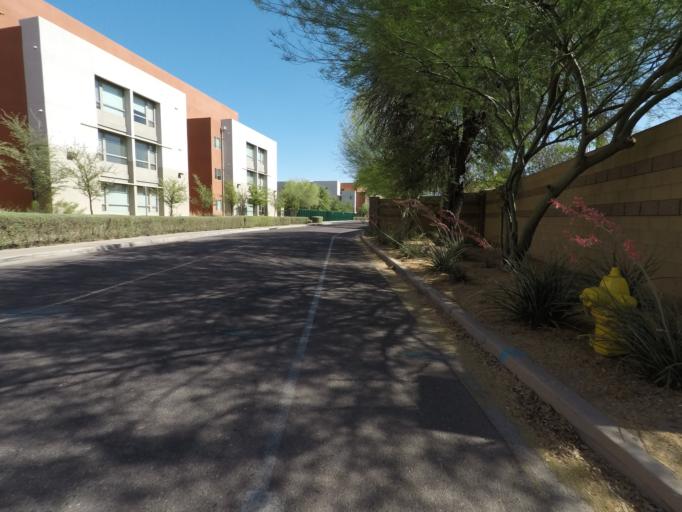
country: US
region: Arizona
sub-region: Maricopa County
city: Tempe Junction
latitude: 33.4138
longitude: -111.9307
